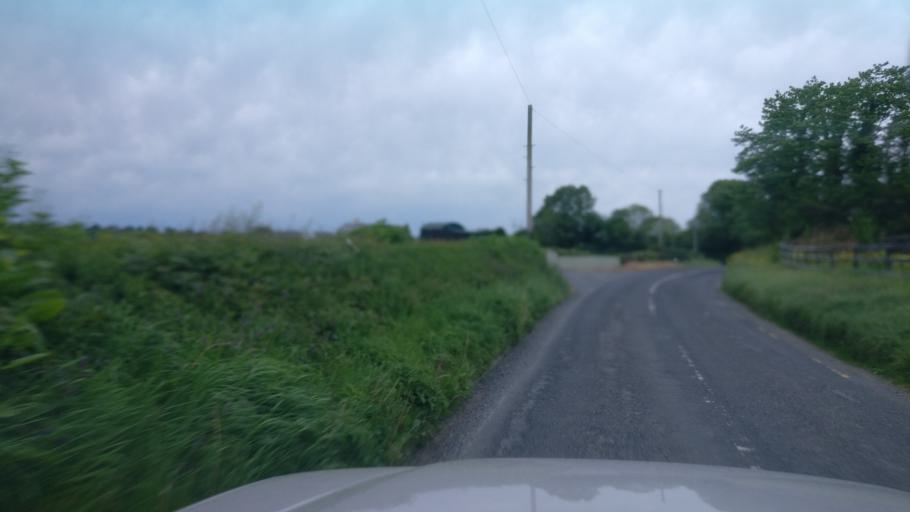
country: IE
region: Connaught
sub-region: County Galway
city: Portumna
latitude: 53.1158
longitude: -8.3033
